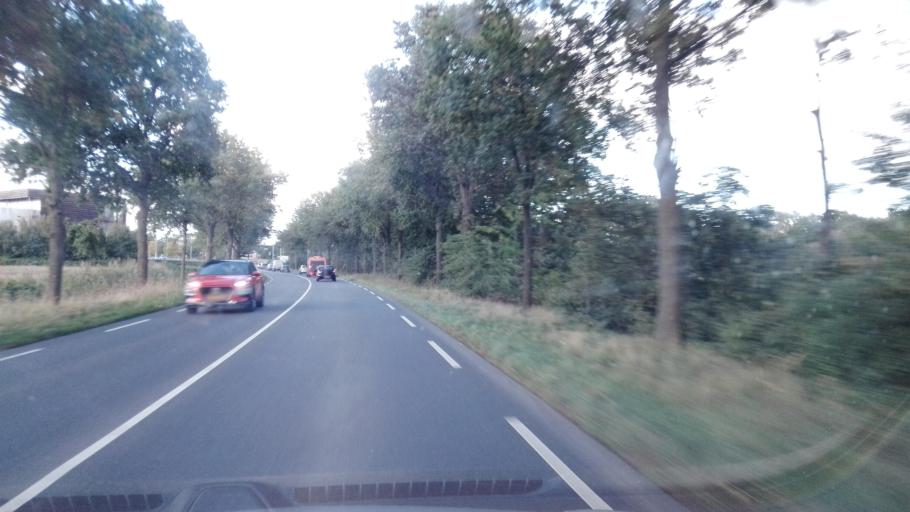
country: NL
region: Limburg
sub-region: Gemeente Venlo
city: Venlo
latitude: 51.3959
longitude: 6.1385
